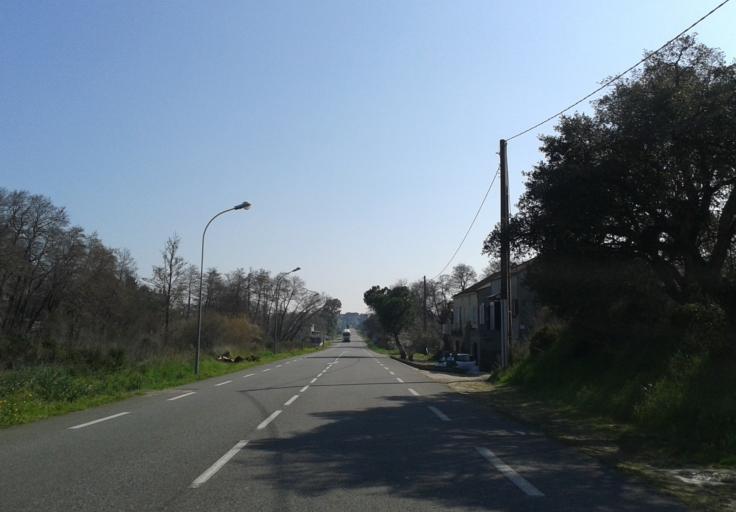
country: FR
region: Corsica
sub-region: Departement de la Haute-Corse
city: Linguizzetta
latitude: 42.2113
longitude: 9.5339
